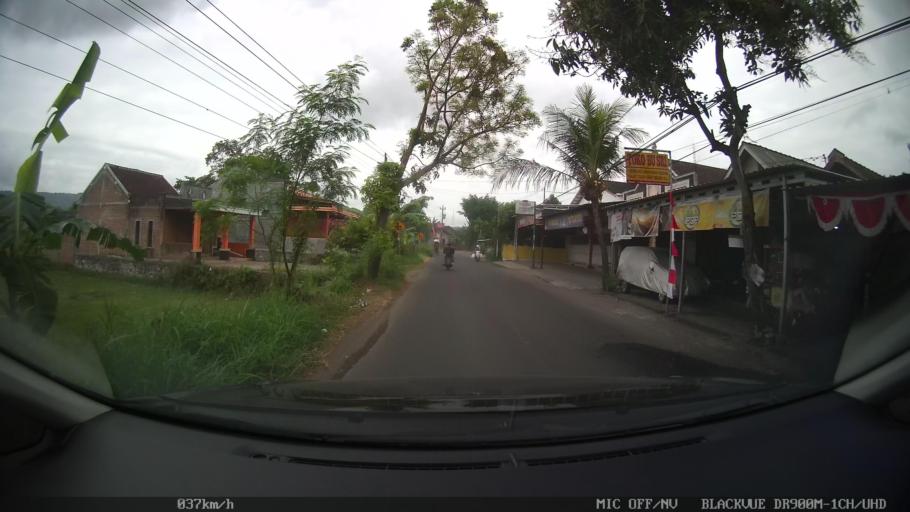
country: ID
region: Daerah Istimewa Yogyakarta
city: Sewon
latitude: -7.8721
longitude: 110.4073
